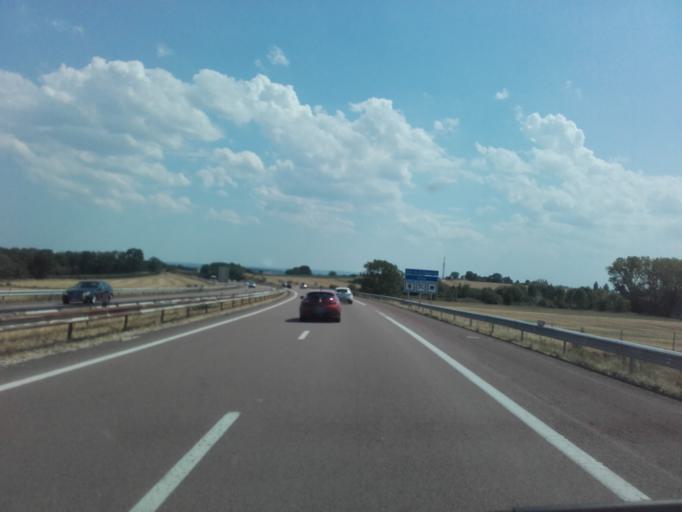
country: FR
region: Bourgogne
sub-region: Departement de l'Yonne
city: Avallon
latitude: 47.5636
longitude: 3.9422
